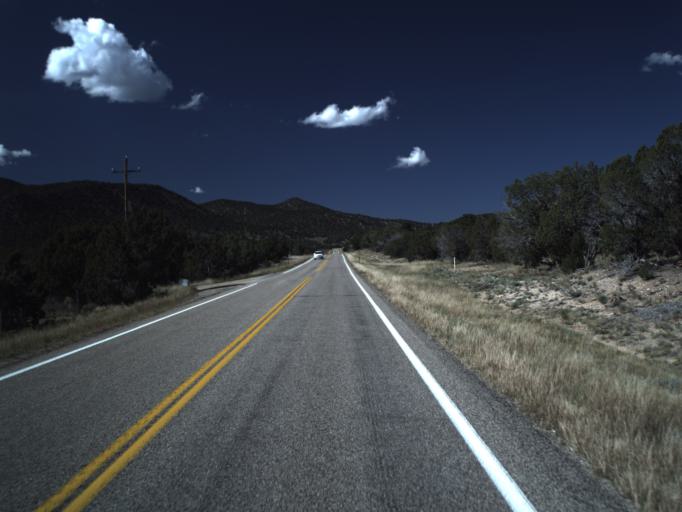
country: US
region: Utah
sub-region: Iron County
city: Cedar City
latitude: 37.6424
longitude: -113.2520
